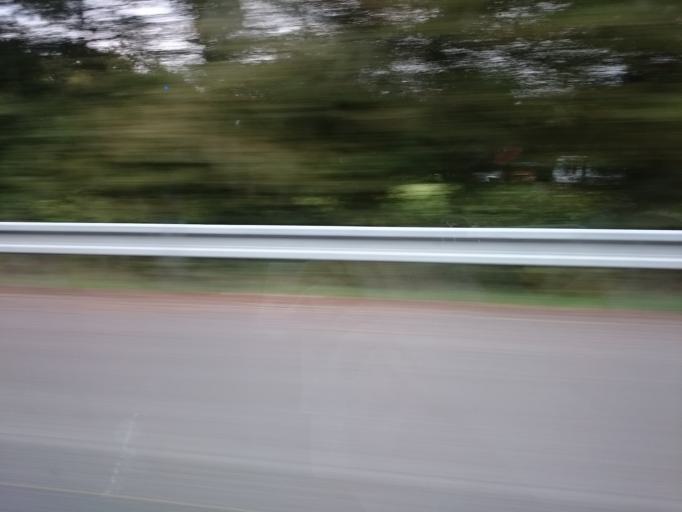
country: FR
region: Brittany
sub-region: Departement du Morbihan
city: Landevant
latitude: 47.7535
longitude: -3.1119
